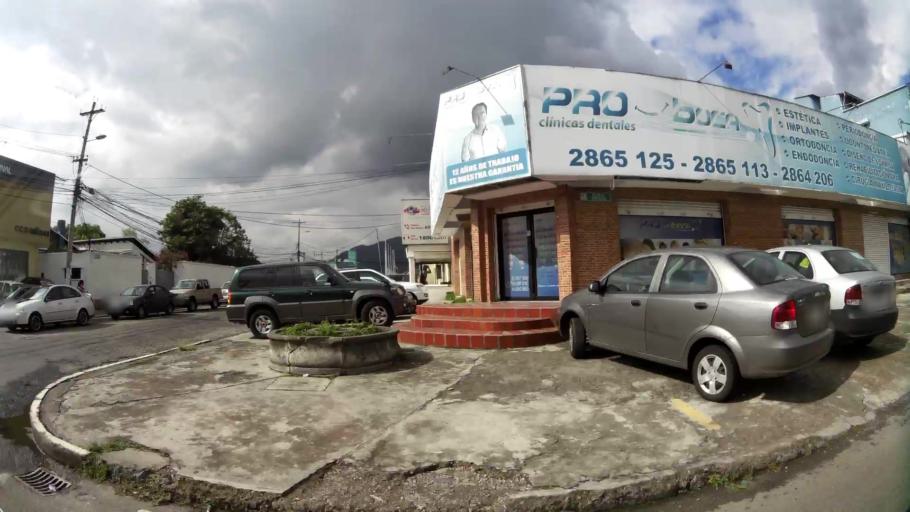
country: EC
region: Pichincha
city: Sangolqui
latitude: -0.3023
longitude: -78.4580
